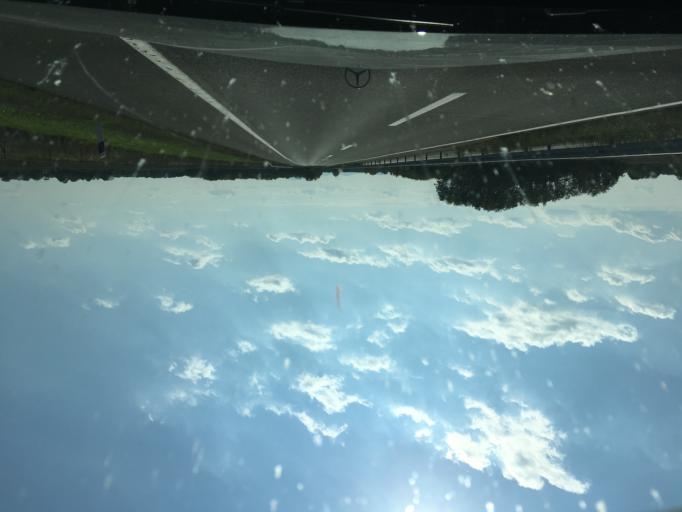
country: HR
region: Medimurska
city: Gardinovec
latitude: 46.4044
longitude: 16.5806
